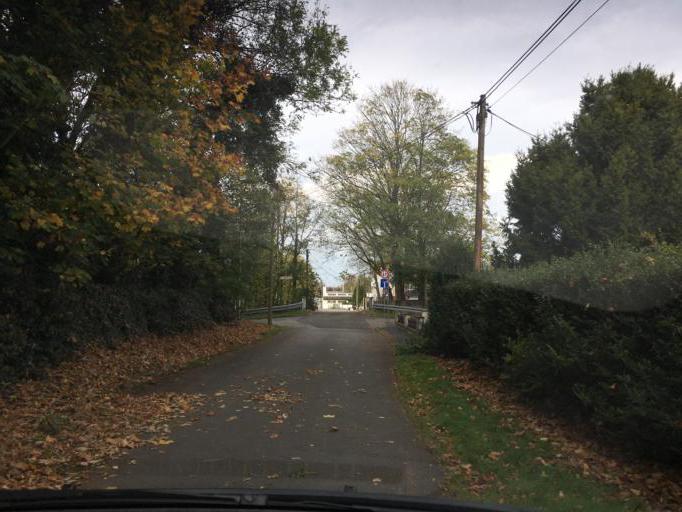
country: DE
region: North Rhine-Westphalia
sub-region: Regierungsbezirk Koln
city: Dueren
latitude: 50.7878
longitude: 6.4749
